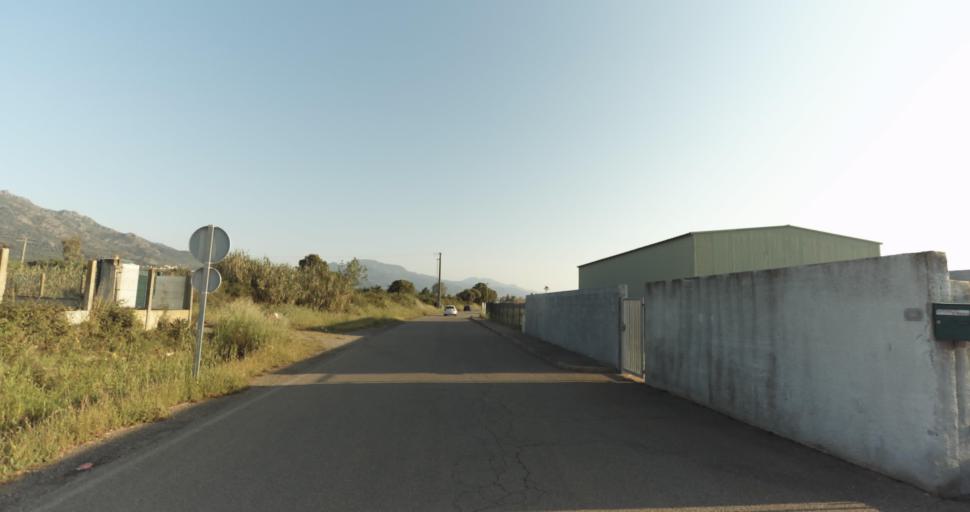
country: FR
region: Corsica
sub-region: Departement de la Haute-Corse
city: Biguglia
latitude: 42.6060
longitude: 9.4441
